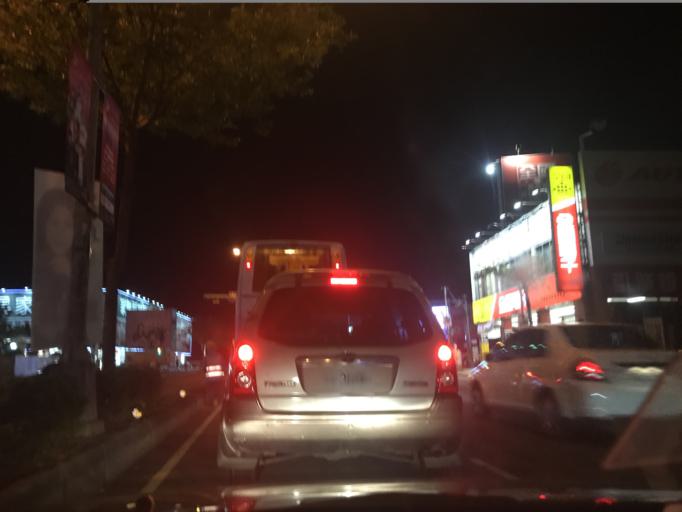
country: TW
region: Taiwan
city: Daxi
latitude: 24.9408
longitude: 121.2163
